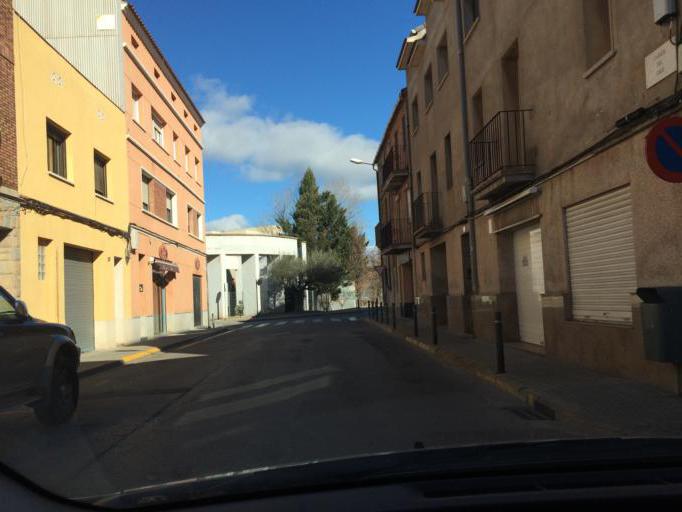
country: ES
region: Catalonia
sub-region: Provincia de Barcelona
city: Manresa
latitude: 41.7377
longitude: 1.8214
